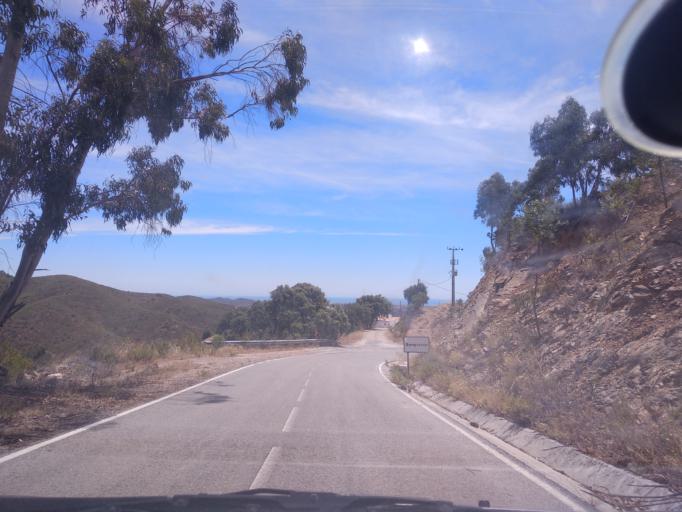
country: PT
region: Faro
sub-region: Sao Bras de Alportel
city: Sao Bras de Alportel
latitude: 37.1943
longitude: -7.7977
